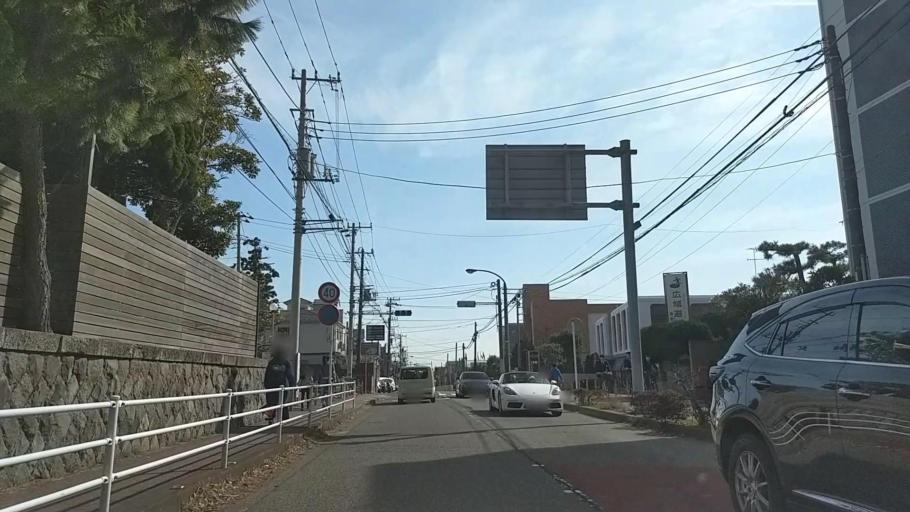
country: JP
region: Kanagawa
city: Fujisawa
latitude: 35.3267
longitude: 139.4531
